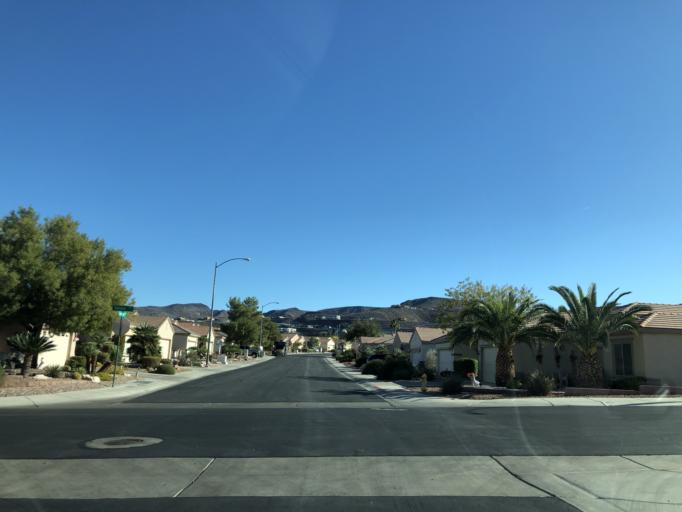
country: US
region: Nevada
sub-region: Clark County
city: Whitney
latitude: 36.0017
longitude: -115.0733
